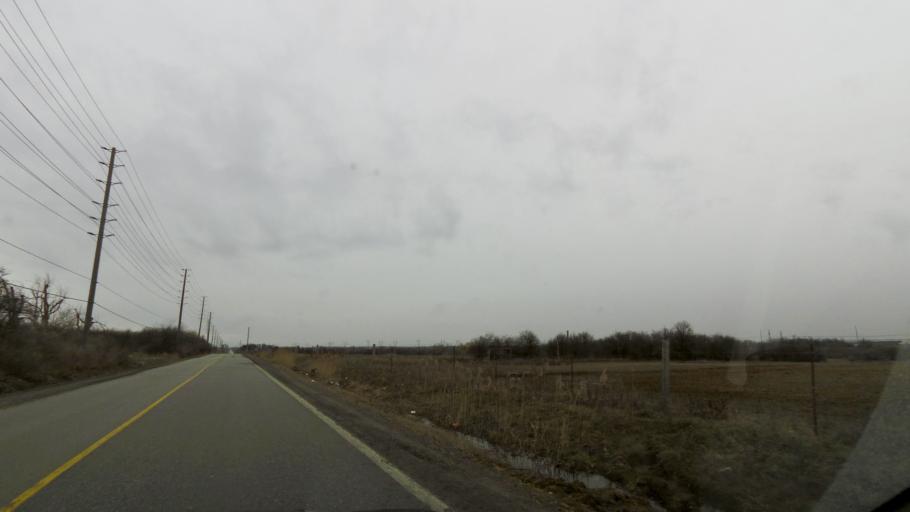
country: CA
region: Ontario
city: Brampton
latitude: 43.7885
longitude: -79.6515
